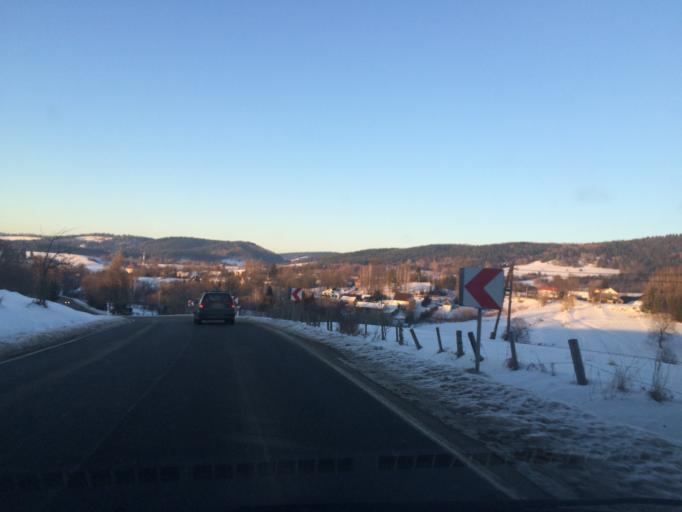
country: PL
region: Subcarpathian Voivodeship
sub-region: Powiat bieszczadzki
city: Czarna
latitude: 49.3166
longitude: 22.6729
